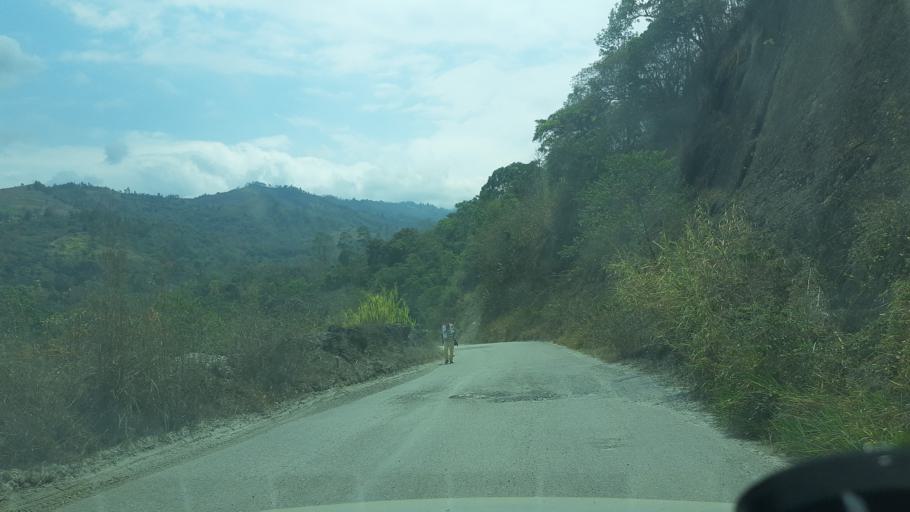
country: CO
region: Boyaca
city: Somondoco
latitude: 5.0119
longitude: -73.3792
